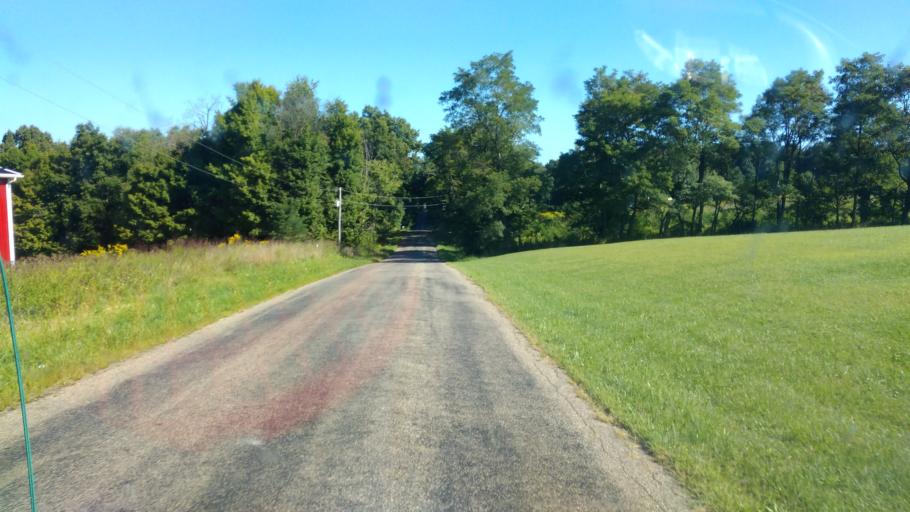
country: US
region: Ohio
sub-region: Knox County
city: Mount Vernon
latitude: 40.4529
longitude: -82.4351
